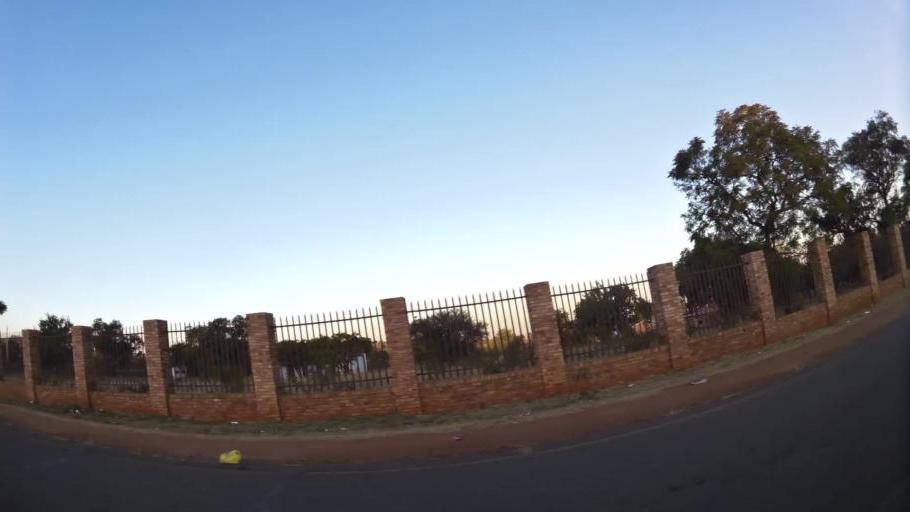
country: ZA
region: North-West
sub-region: Bojanala Platinum District Municipality
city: Rustenburg
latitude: -25.6339
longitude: 27.2021
